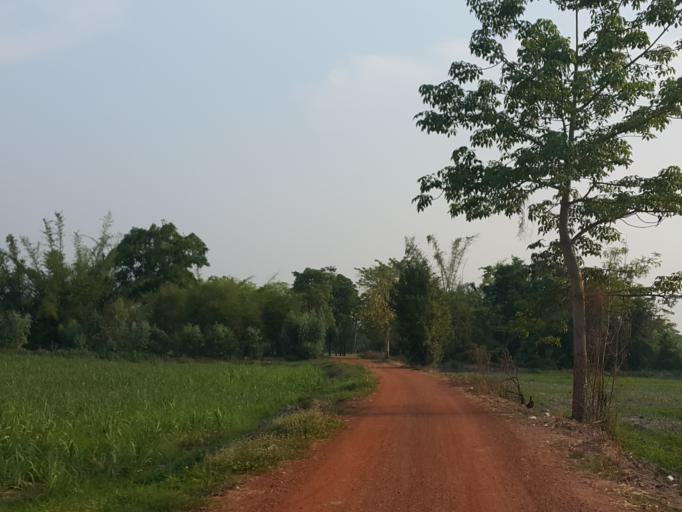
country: TH
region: Uthai Thani
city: Huai Khot
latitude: 15.3184
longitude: 99.6735
